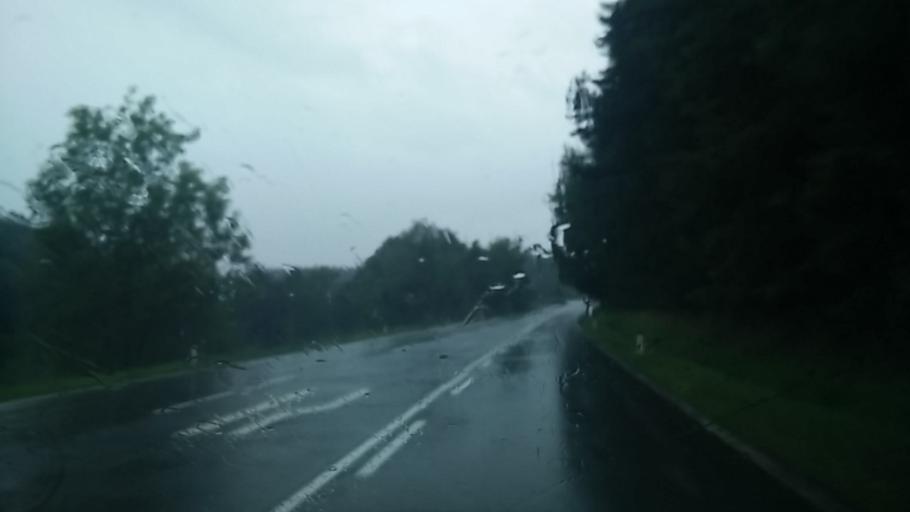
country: AT
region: Carinthia
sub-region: Politischer Bezirk Villach Land
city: Wernberg
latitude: 46.6141
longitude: 13.9660
